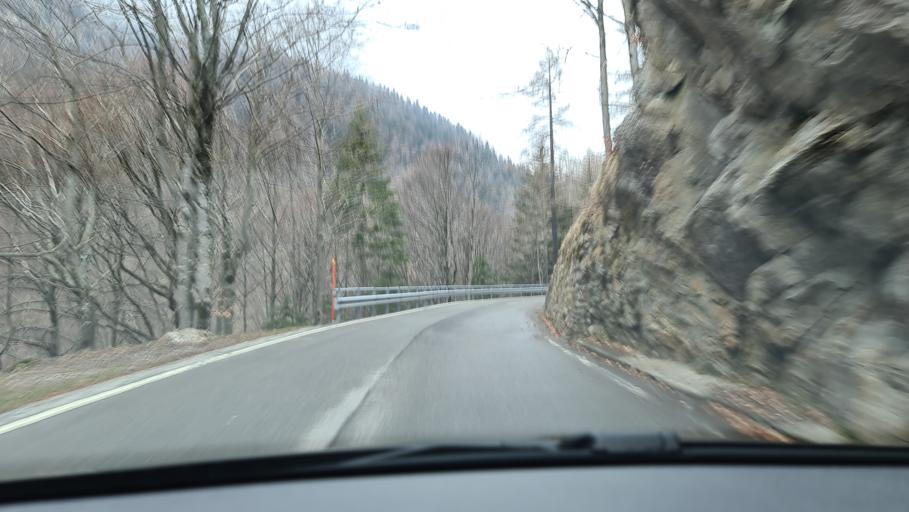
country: CH
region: Ticino
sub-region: Leventina District
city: Airolo
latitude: 46.4401
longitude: 8.6607
